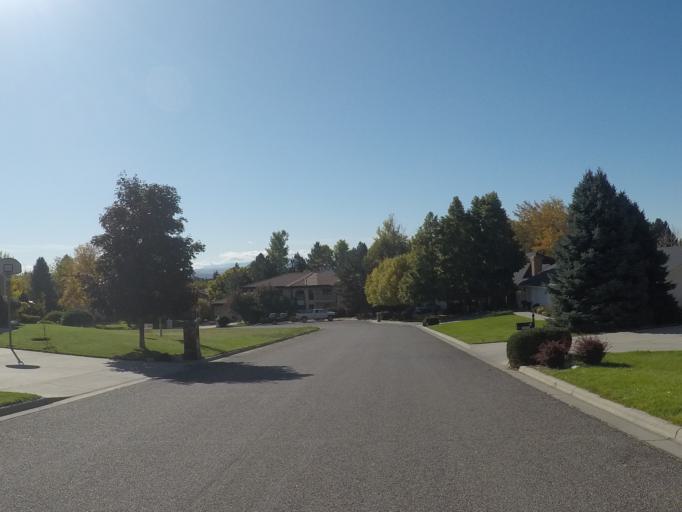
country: US
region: Montana
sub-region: Yellowstone County
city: Billings
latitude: 45.8009
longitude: -108.5888
